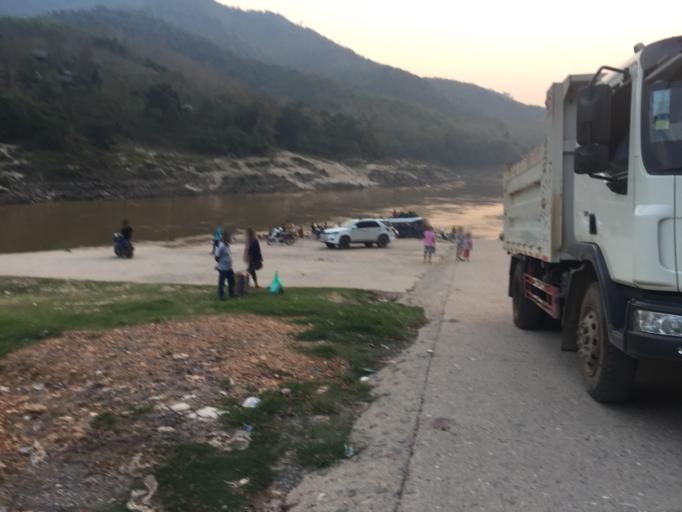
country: TH
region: Nan
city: Chaloem Phra Kiat
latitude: 19.8923
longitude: 101.1295
